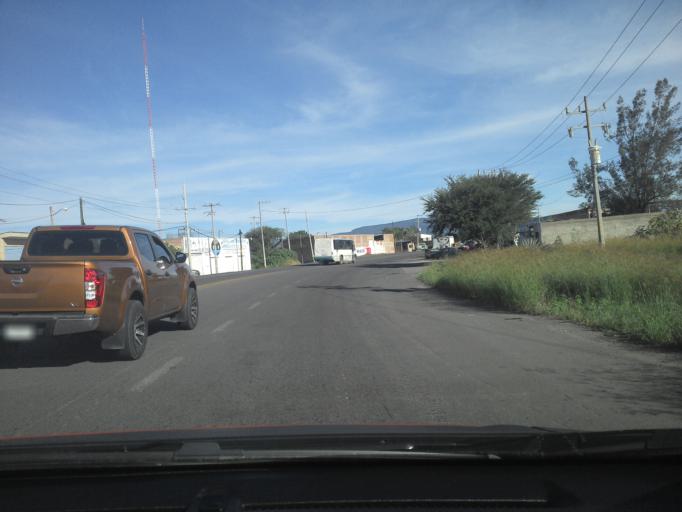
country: MX
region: Jalisco
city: El Refugio
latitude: 20.6667
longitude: -103.7396
